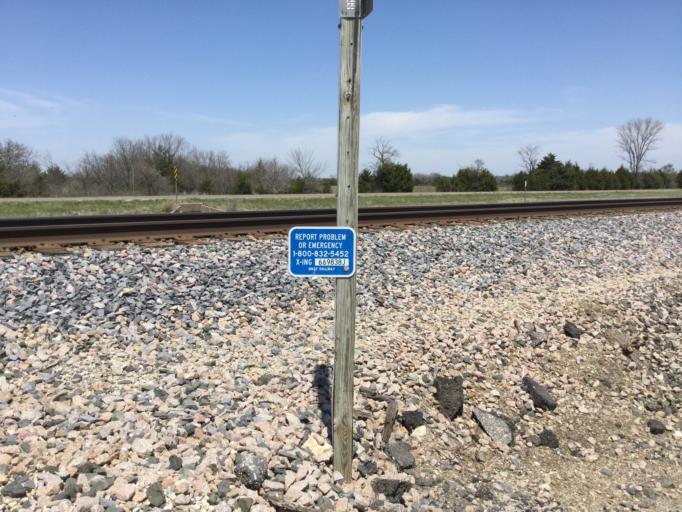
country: US
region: Kansas
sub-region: Bourbon County
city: Fort Scott
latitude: 37.7465
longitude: -94.7311
